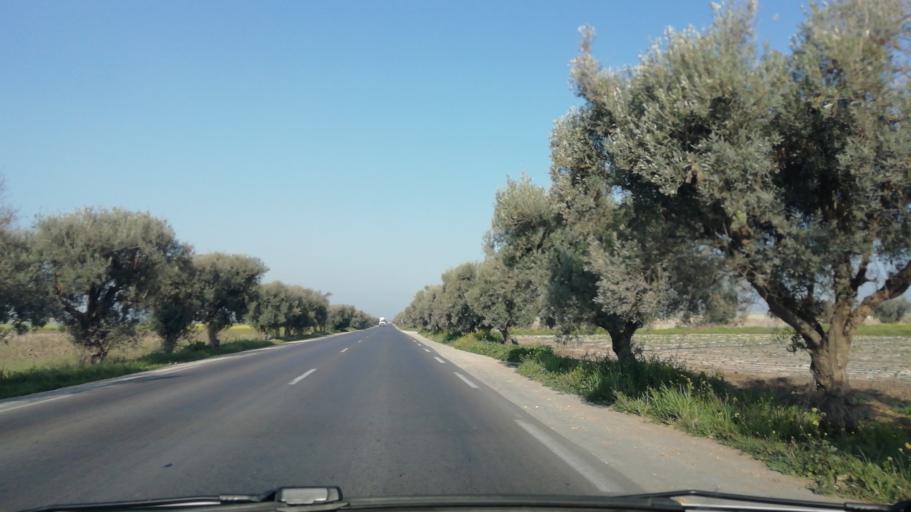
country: DZ
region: Mostaganem
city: Mostaganem
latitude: 35.7464
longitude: 0.1387
